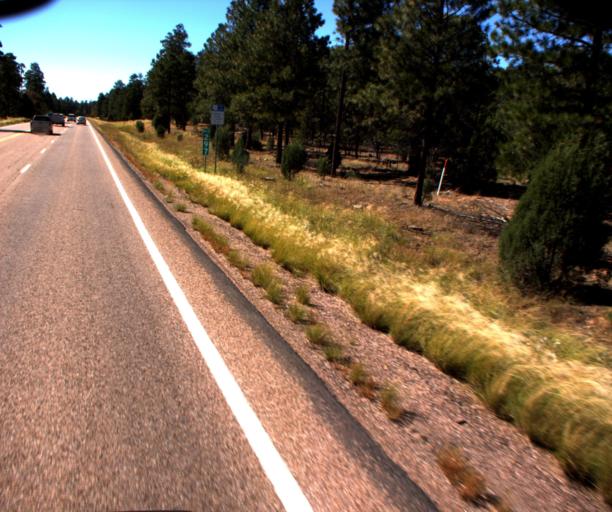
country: US
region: Arizona
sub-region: Navajo County
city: Heber-Overgaard
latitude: 34.3801
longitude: -110.6731
